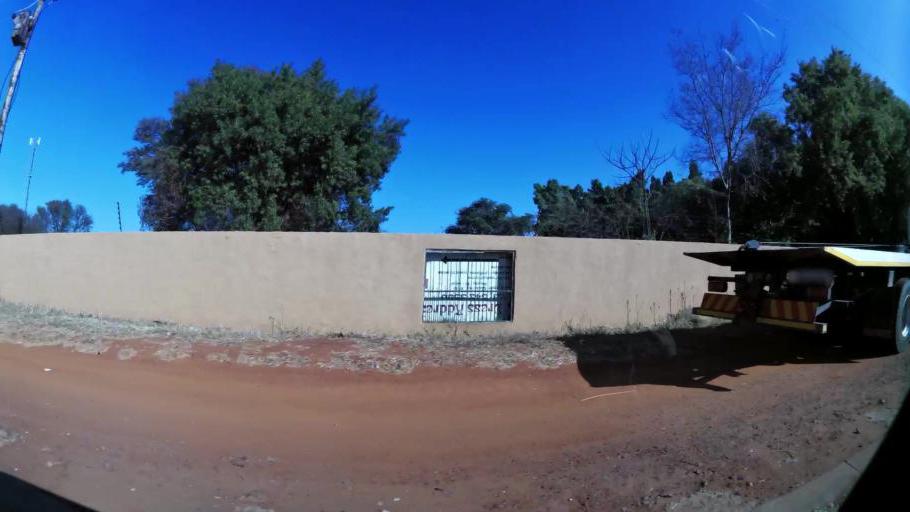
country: ZA
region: Gauteng
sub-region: City of Tshwane Metropolitan Municipality
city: Pretoria
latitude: -25.6549
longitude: 28.1312
